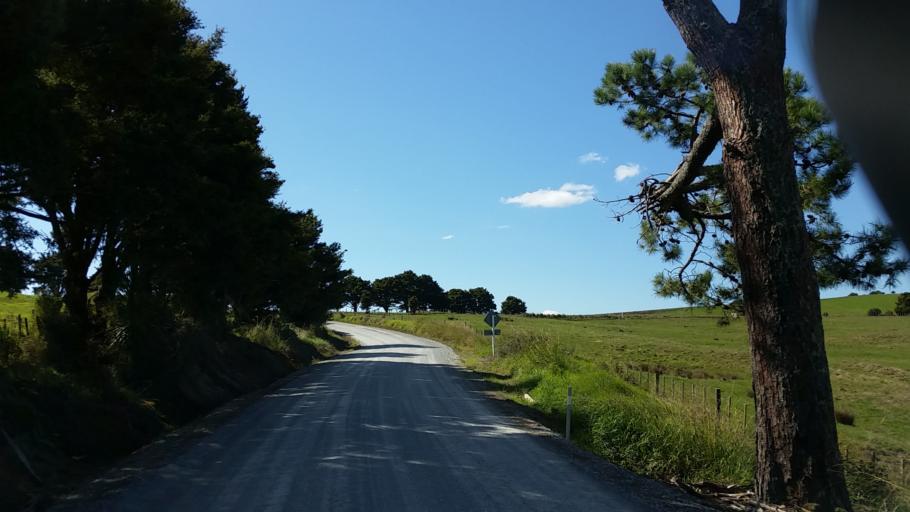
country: NZ
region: Northland
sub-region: Whangarei
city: Maungatapere
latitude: -35.6898
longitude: 174.2187
